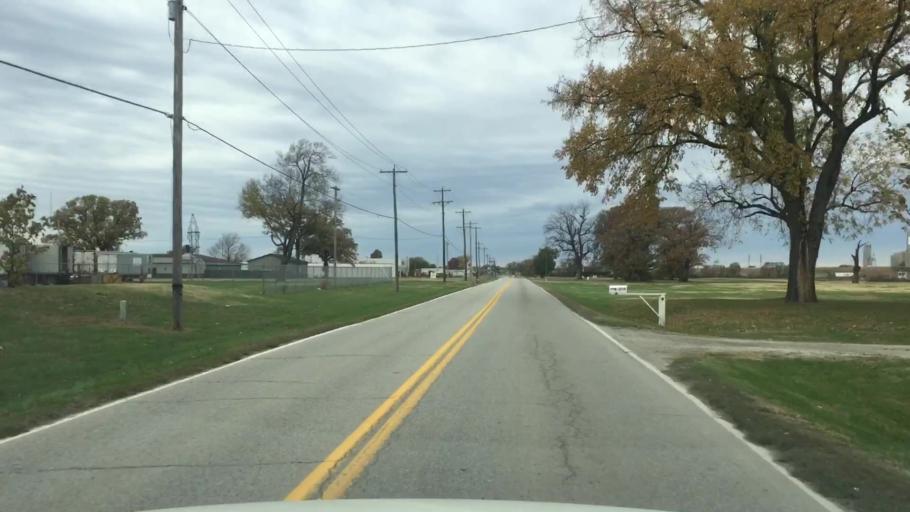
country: US
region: Kansas
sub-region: Shawnee County
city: Topeka
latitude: 39.0815
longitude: -95.7194
